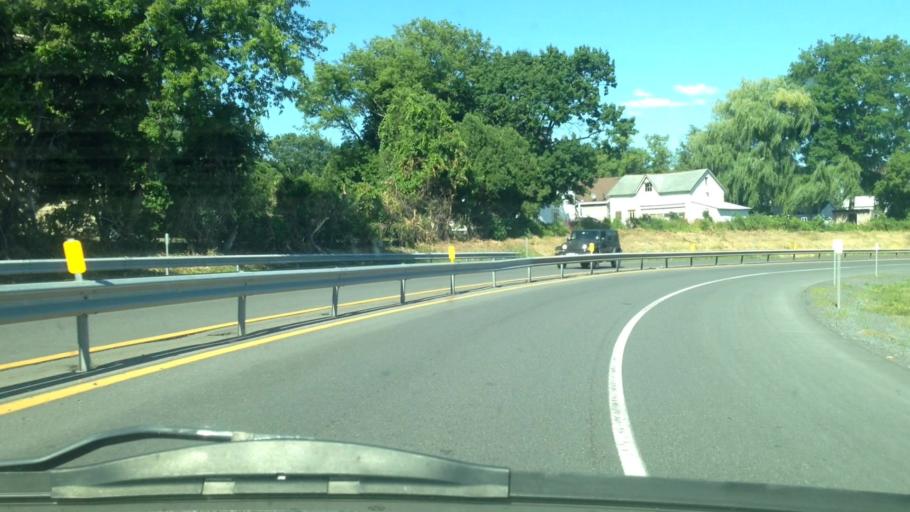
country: US
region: New York
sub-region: Oneida County
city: Utica
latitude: 43.1135
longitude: -75.2043
